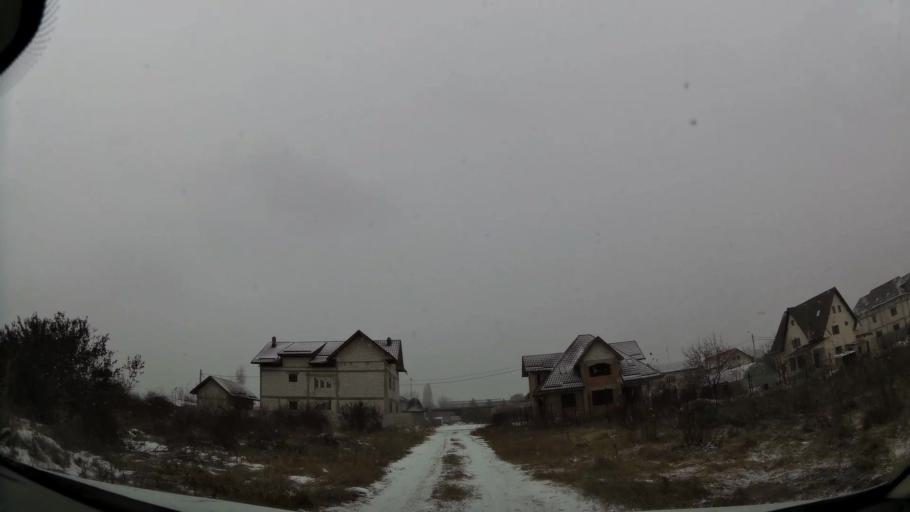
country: RO
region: Dambovita
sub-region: Municipiul Targoviste
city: Targoviste
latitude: 44.9126
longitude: 25.4717
